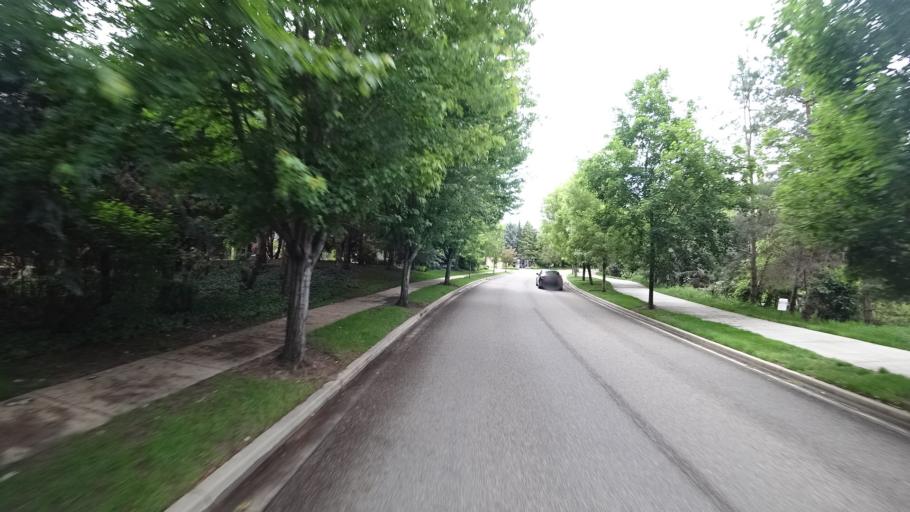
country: US
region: Idaho
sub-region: Ada County
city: Eagle
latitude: 43.6796
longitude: -116.3569
